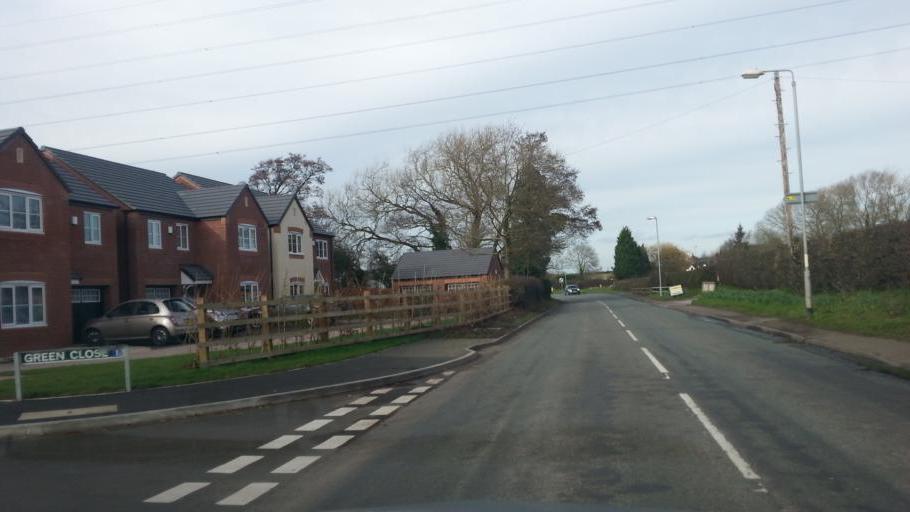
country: GB
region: England
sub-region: Staffordshire
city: Colwich
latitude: 52.8063
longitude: -2.0014
